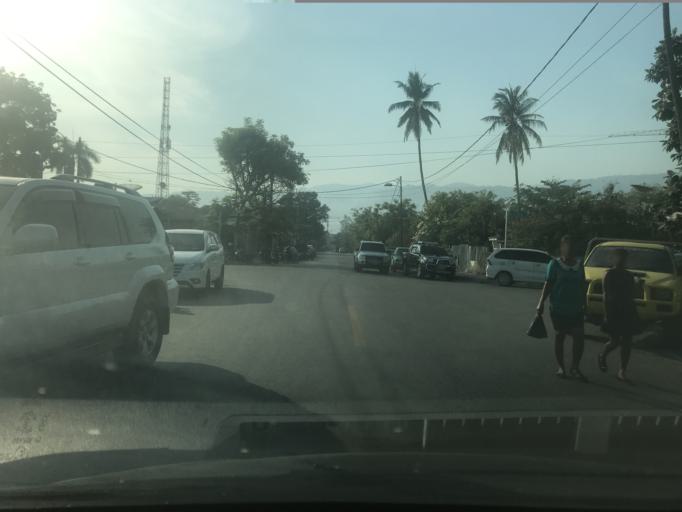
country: TL
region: Dili
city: Dili
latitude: -8.5513
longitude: 125.5698
